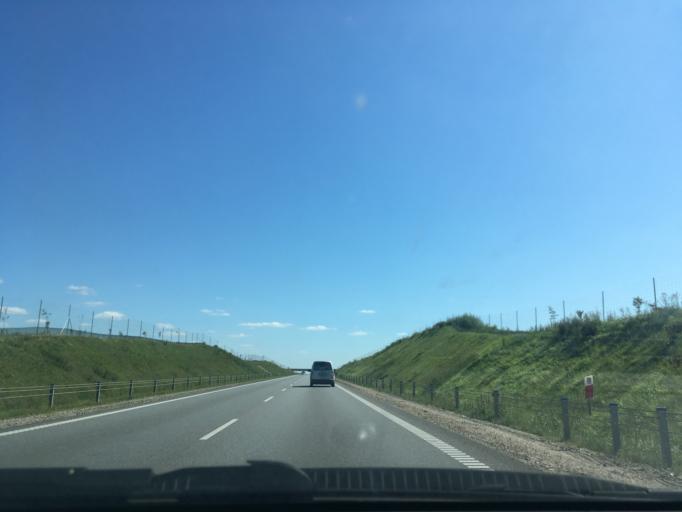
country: PL
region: Podlasie
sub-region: Powiat suwalski
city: Raczki
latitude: 53.9071
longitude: 22.8440
